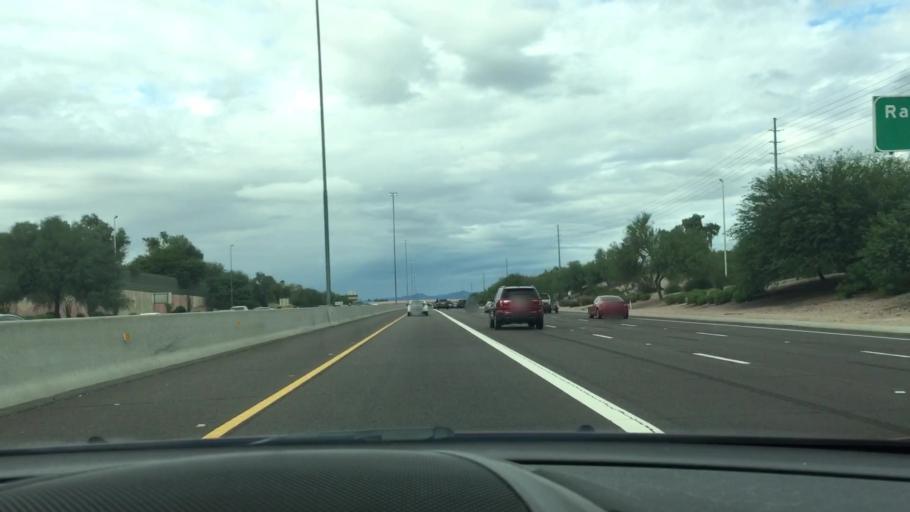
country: US
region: Arizona
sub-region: Maricopa County
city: Paradise Valley
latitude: 33.5976
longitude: -111.8931
